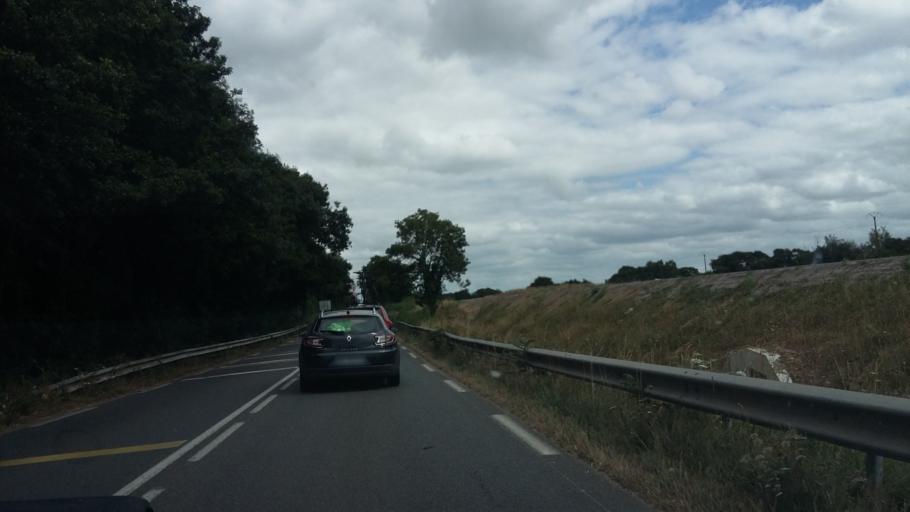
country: FR
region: Pays de la Loire
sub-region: Departement de la Vendee
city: Saint-Christophe-du-Ligneron
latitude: 46.8313
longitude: -1.8145
